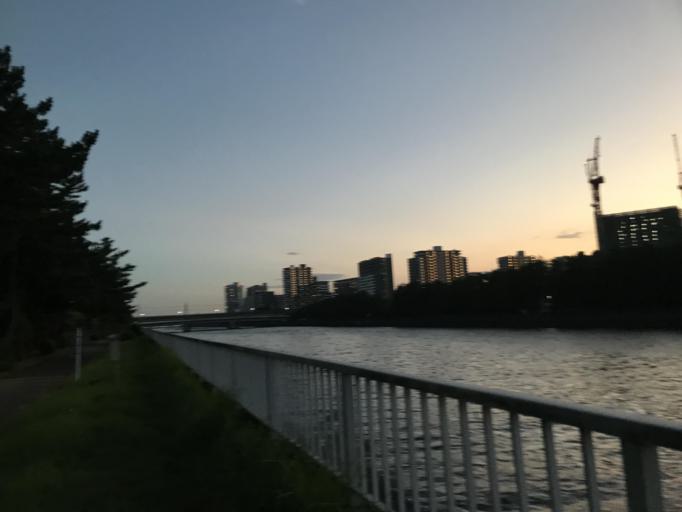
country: BR
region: Alagoas
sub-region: Porto Real Do Colegio
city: Porto Real do Colegio
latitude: -10.1762
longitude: -36.7803
